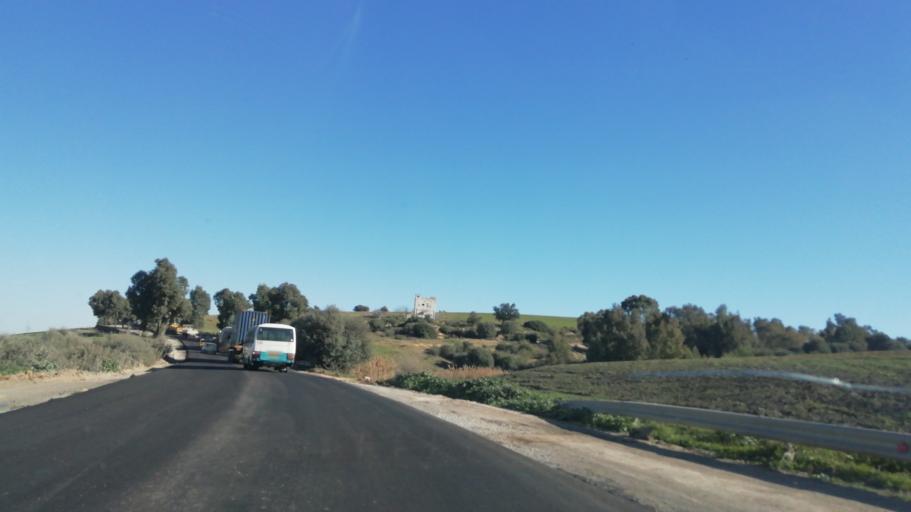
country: DZ
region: Relizane
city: Smala
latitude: 35.6607
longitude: 0.8118
